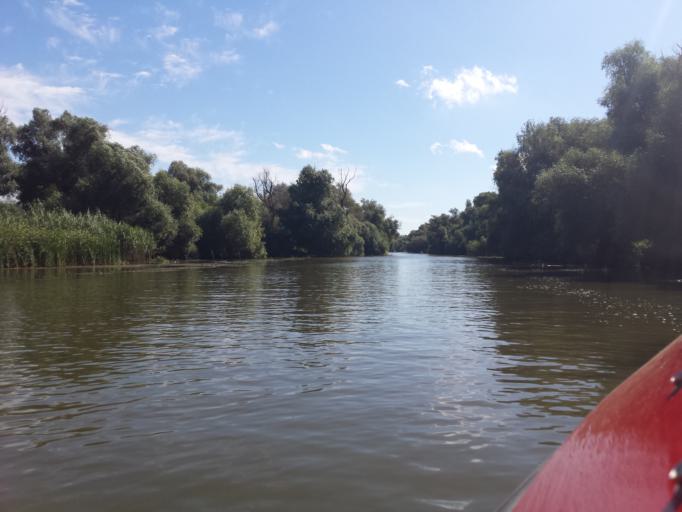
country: RO
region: Tulcea
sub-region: Comuna Mahmudia
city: Mahmudia
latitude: 45.2146
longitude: 29.1843
